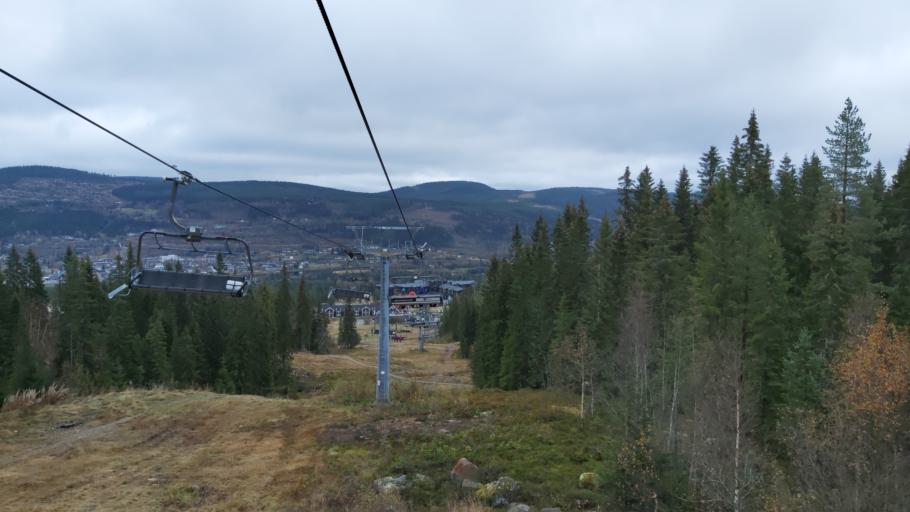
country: NO
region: Hedmark
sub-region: Trysil
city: Innbygda
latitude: 61.3081
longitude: 12.2290
